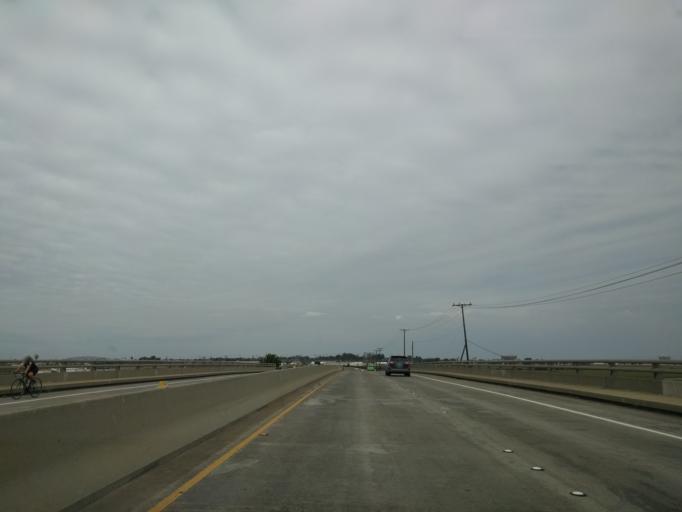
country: US
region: California
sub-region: Orange County
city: Seal Beach
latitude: 33.7316
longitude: -118.0847
